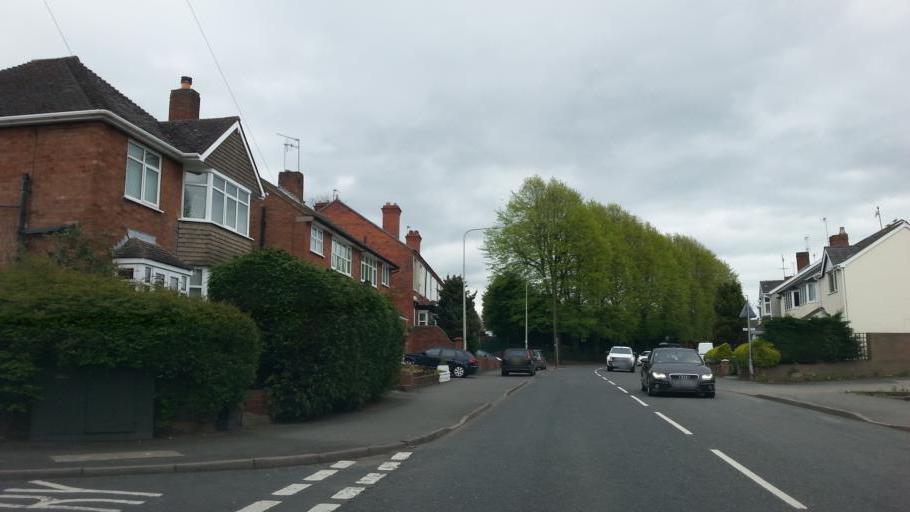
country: GB
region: England
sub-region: Dudley
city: Kingswinford
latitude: 52.4813
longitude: -2.1654
